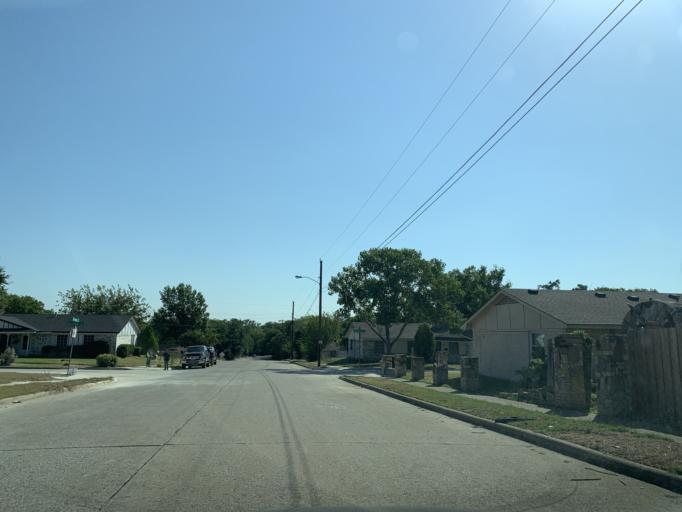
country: US
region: Texas
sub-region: Dallas County
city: Hutchins
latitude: 32.6663
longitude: -96.7533
